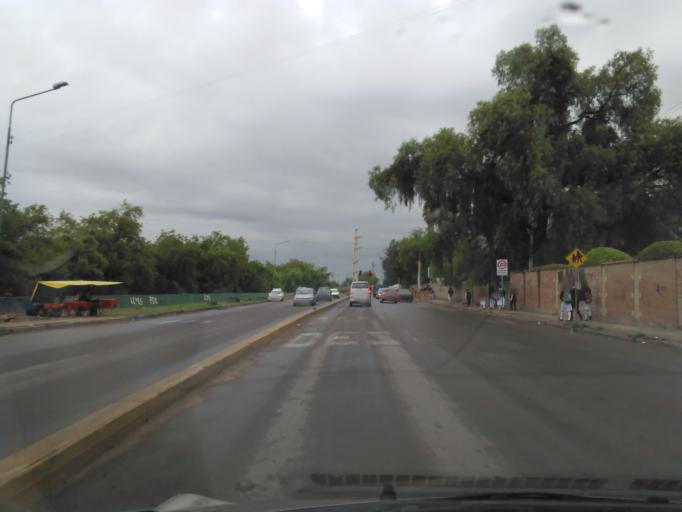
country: BO
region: Cochabamba
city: Cochabamba
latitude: -17.3949
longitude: -66.1677
